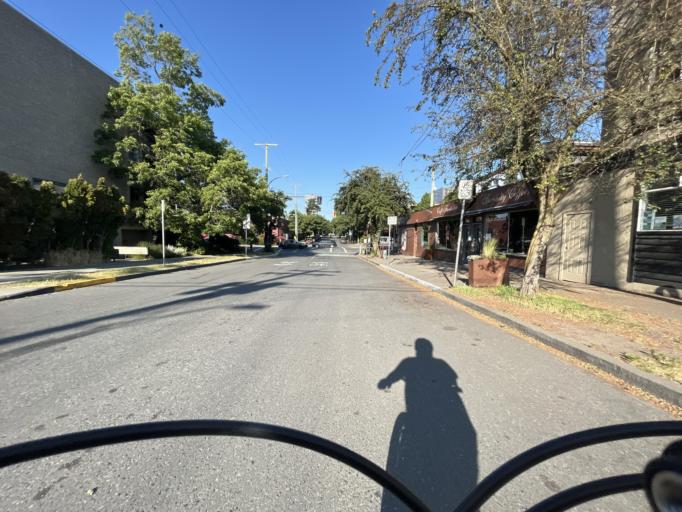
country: CA
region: British Columbia
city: Victoria
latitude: 48.4374
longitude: -123.3593
